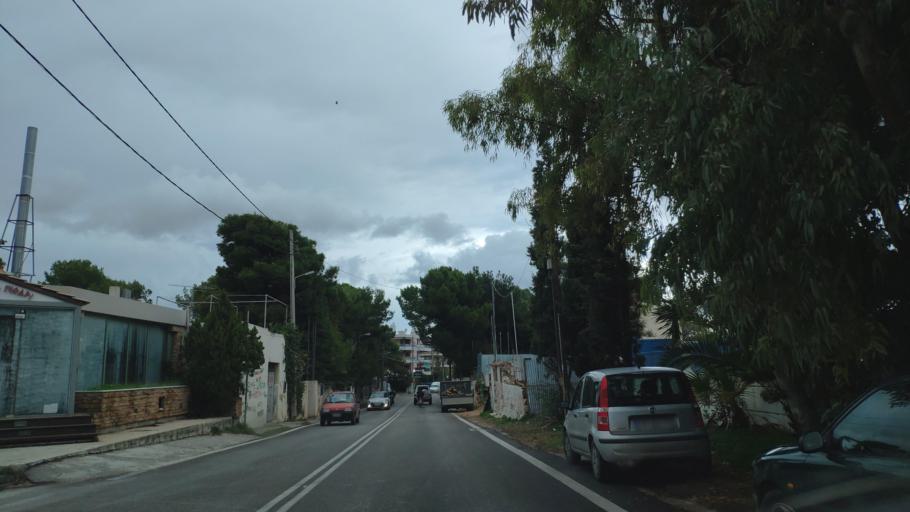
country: GR
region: Attica
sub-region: Nomarchia Anatolikis Attikis
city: Artemida
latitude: 37.9660
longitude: 24.0061
